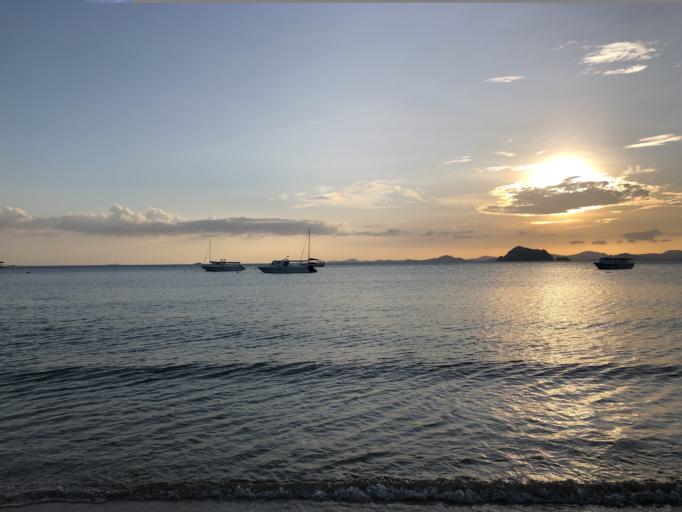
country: TH
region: Phangnga
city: Ban Phru Nai
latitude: 7.9820
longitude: 98.5683
